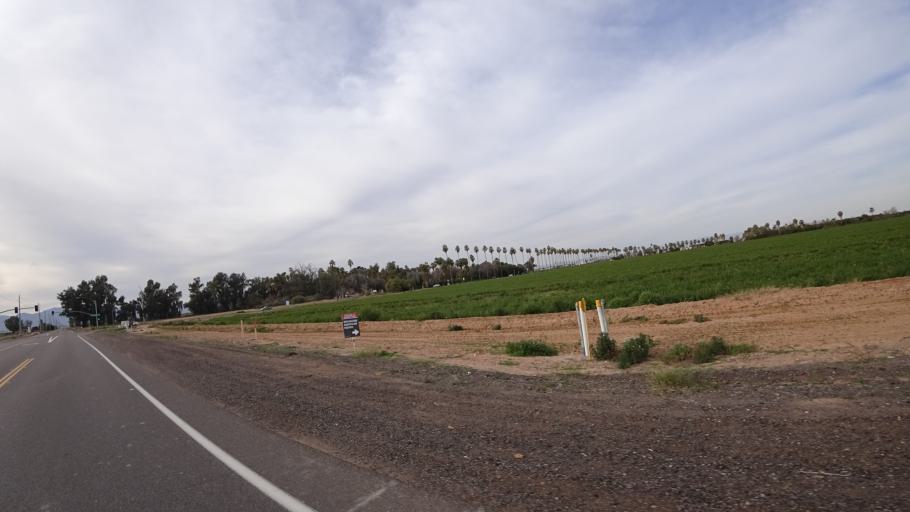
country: US
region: Arizona
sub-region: Maricopa County
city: El Mirage
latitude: 33.5658
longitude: -112.3574
